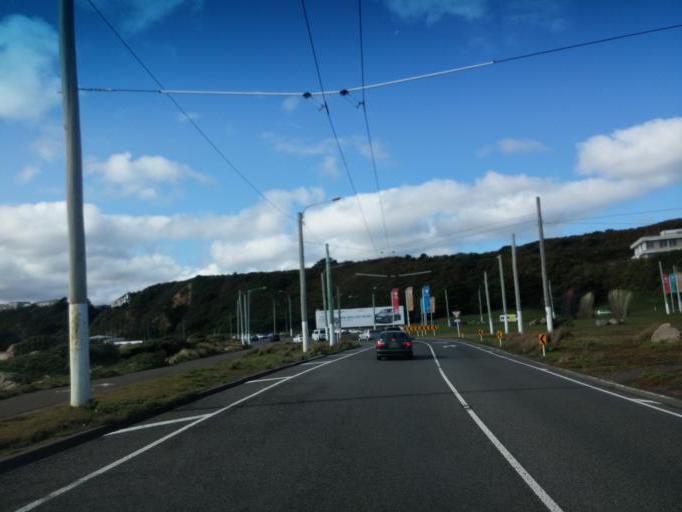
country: NZ
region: Wellington
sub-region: Wellington City
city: Wellington
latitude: -41.3167
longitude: 174.8078
